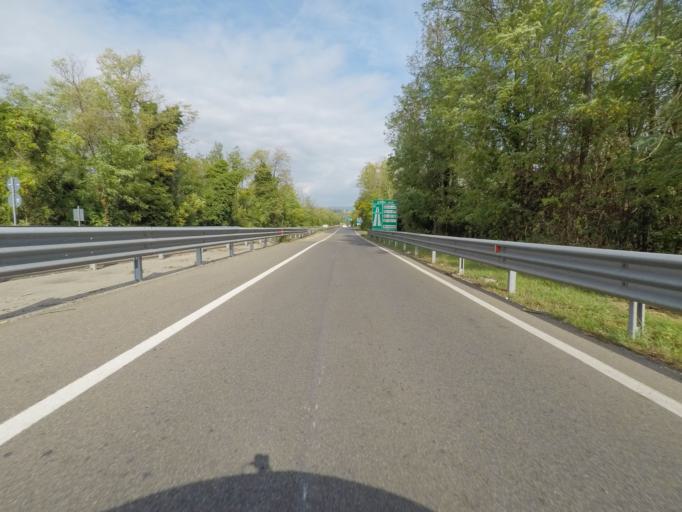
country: IT
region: Tuscany
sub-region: Provincia di Siena
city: Belverde
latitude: 43.3507
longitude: 11.3060
